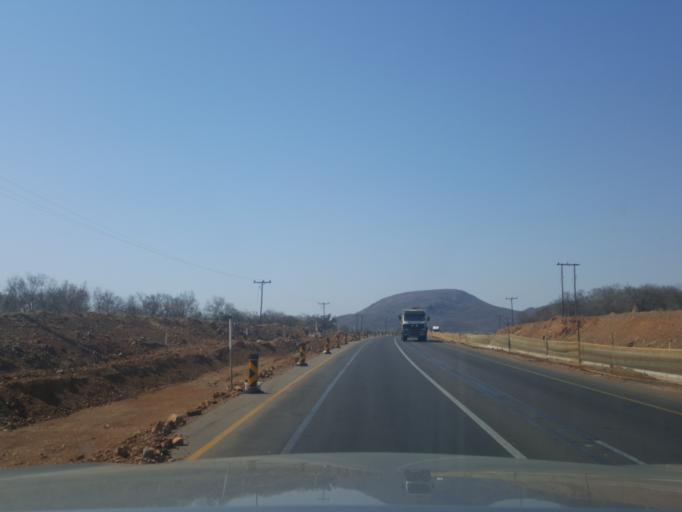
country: BW
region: Kweneng
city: Gabane
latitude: -24.7484
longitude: 25.8290
